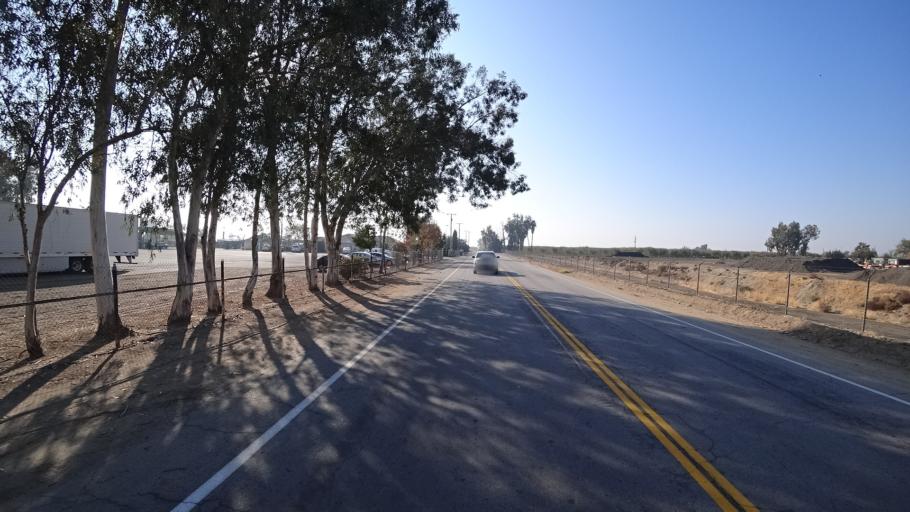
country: US
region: California
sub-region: Kern County
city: Greenfield
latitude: 35.2612
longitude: -119.0257
